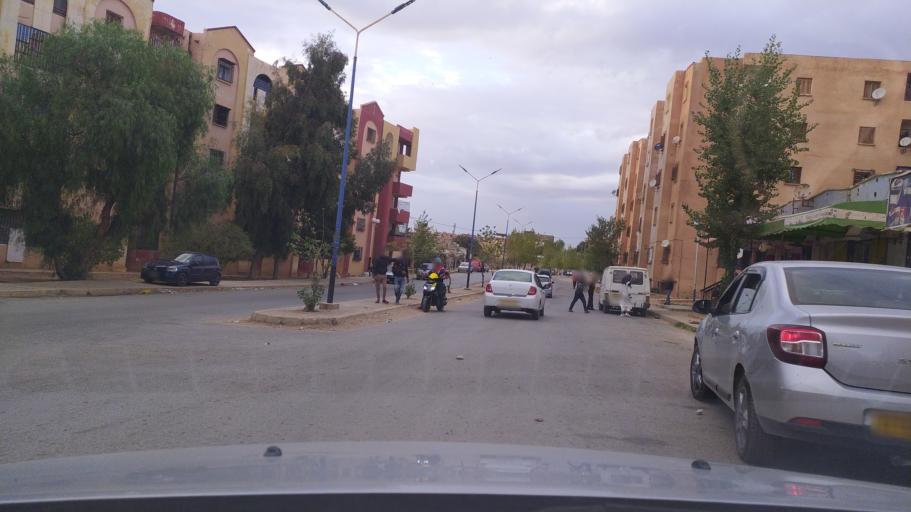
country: DZ
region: Tiaret
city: Frenda
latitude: 35.0568
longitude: 1.0613
